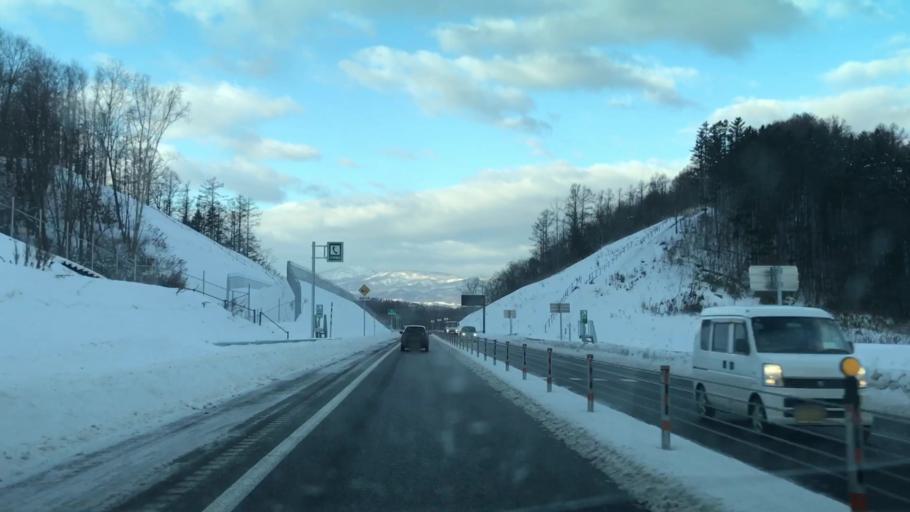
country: JP
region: Hokkaido
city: Otaru
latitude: 43.1955
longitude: 140.8866
